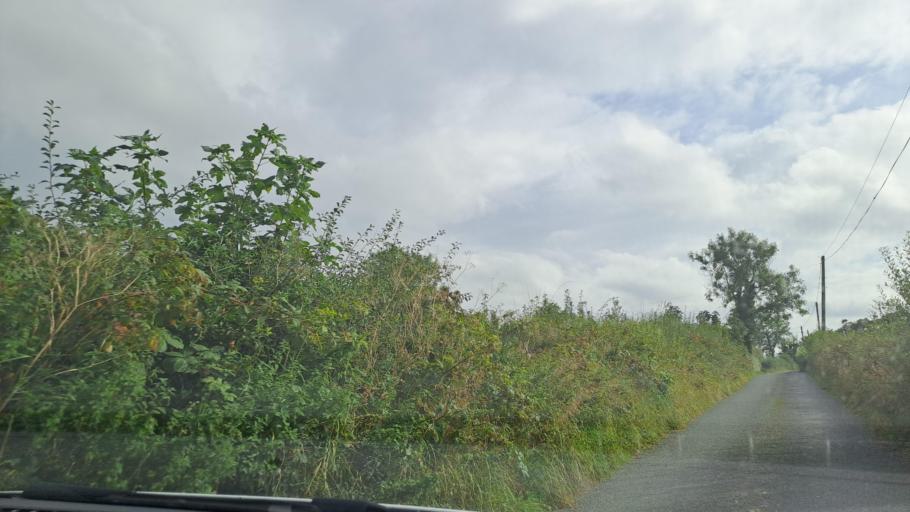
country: IE
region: Ulster
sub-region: An Cabhan
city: Kingscourt
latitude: 53.9846
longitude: -6.8612
